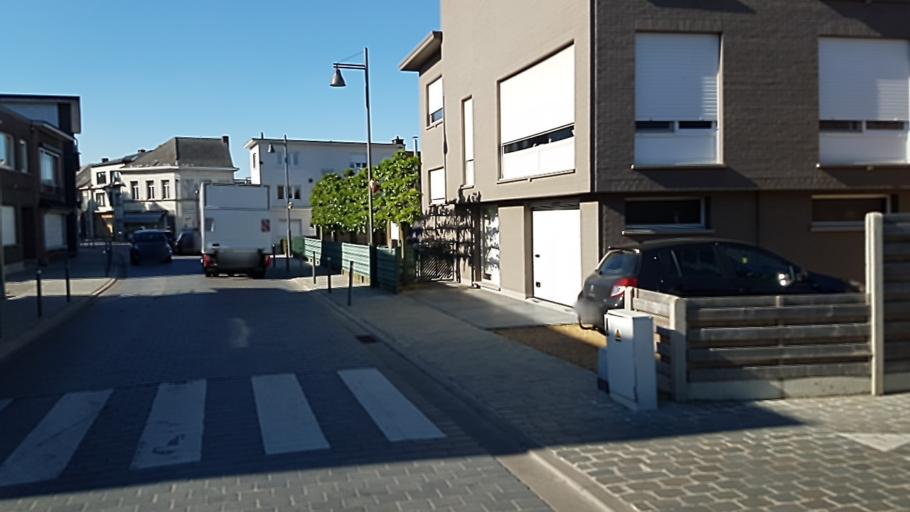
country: BE
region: Flanders
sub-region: Provincie Antwerpen
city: Heist-op-den-Berg
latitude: 51.1021
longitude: 4.7304
